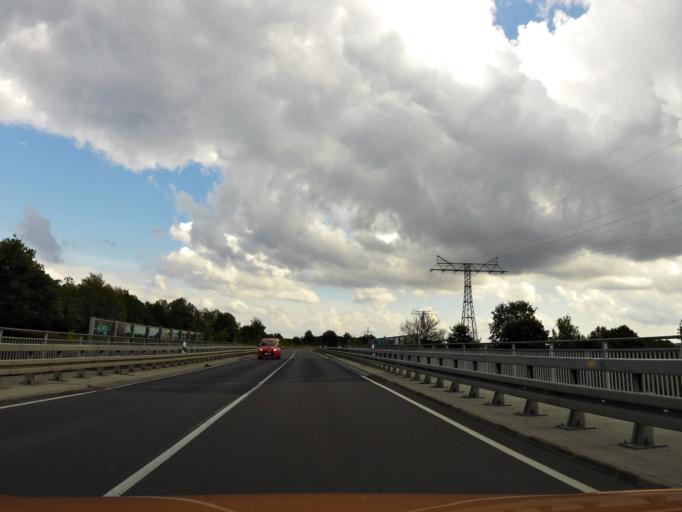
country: DE
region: Brandenburg
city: Wustermark
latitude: 52.4664
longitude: 12.9679
